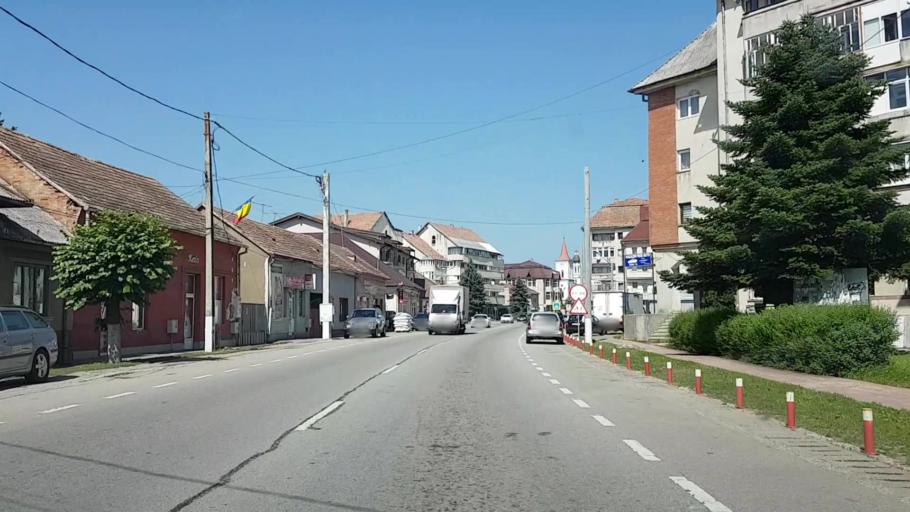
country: RO
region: Bistrita-Nasaud
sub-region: Comuna Beclean
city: Beclean
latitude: 47.1780
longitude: 24.1737
